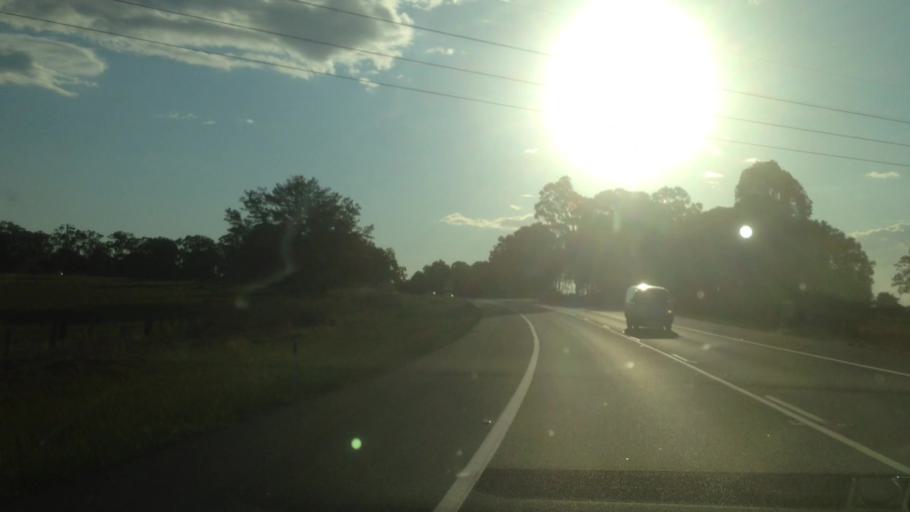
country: AU
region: New South Wales
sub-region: Cessnock
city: Heddon Greta
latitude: -32.8311
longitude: 151.5167
